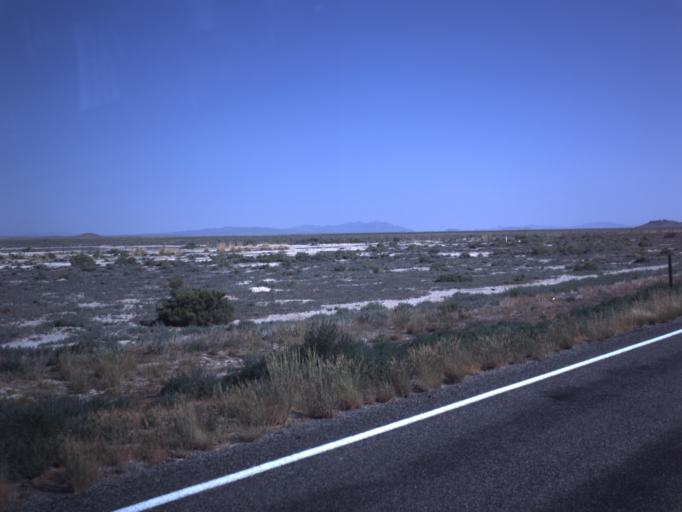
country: US
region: Utah
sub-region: Millard County
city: Delta
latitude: 39.0360
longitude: -112.7732
